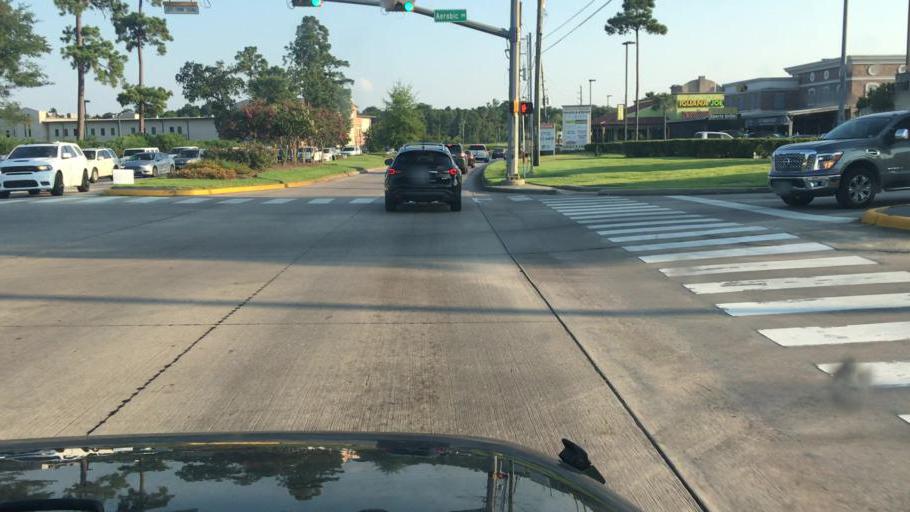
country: US
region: Texas
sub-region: Harris County
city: Atascocita
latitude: 29.9848
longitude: -95.1617
